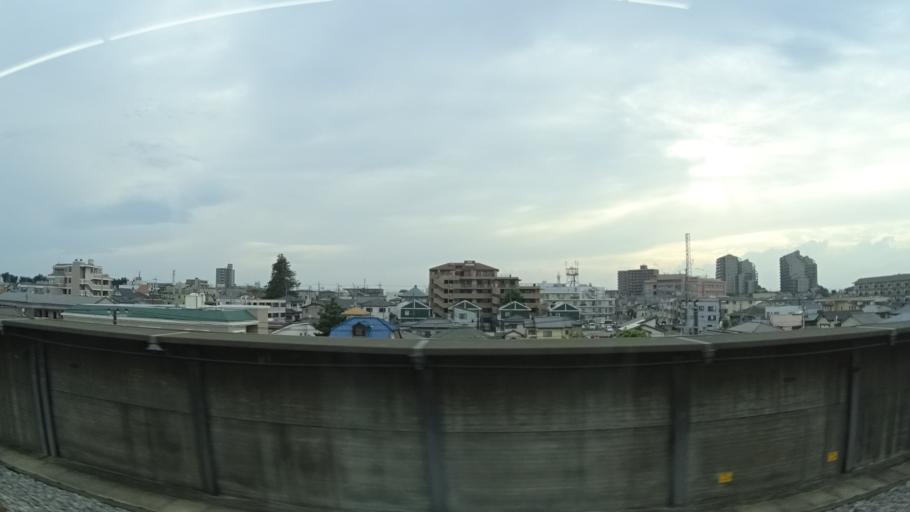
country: JP
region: Saitama
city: Yono
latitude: 35.8736
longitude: 139.6286
